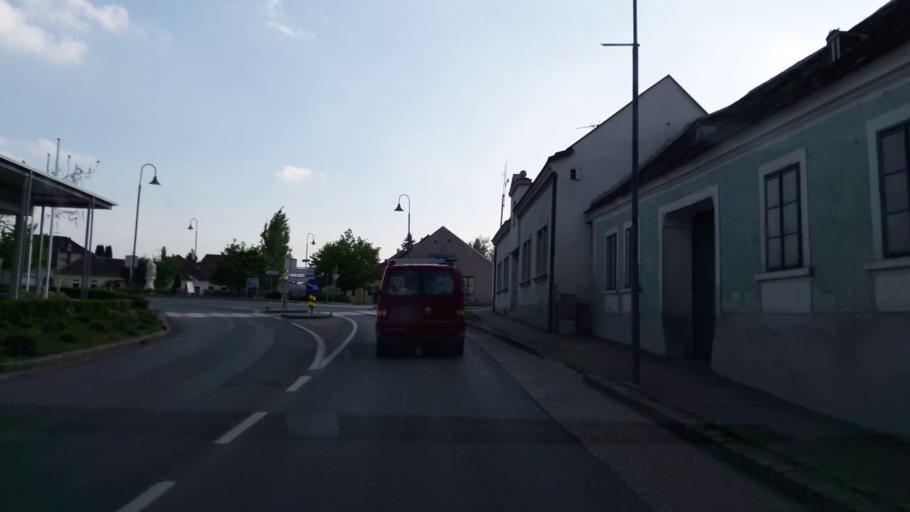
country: AT
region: Lower Austria
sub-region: Politischer Bezirk Hollabrunn
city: Guntersdorf
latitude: 48.6477
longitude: 16.0459
